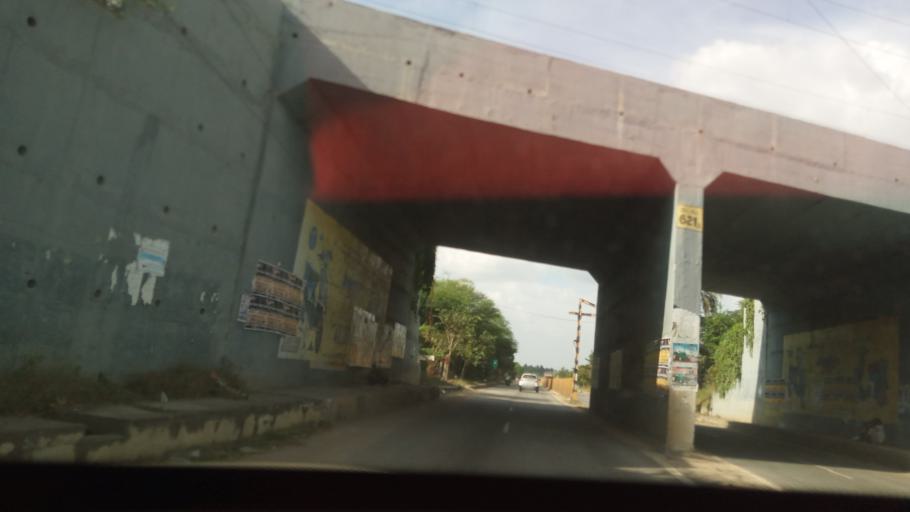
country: IN
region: Karnataka
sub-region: Mandya
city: Maddur
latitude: 12.6144
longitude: 77.0580
